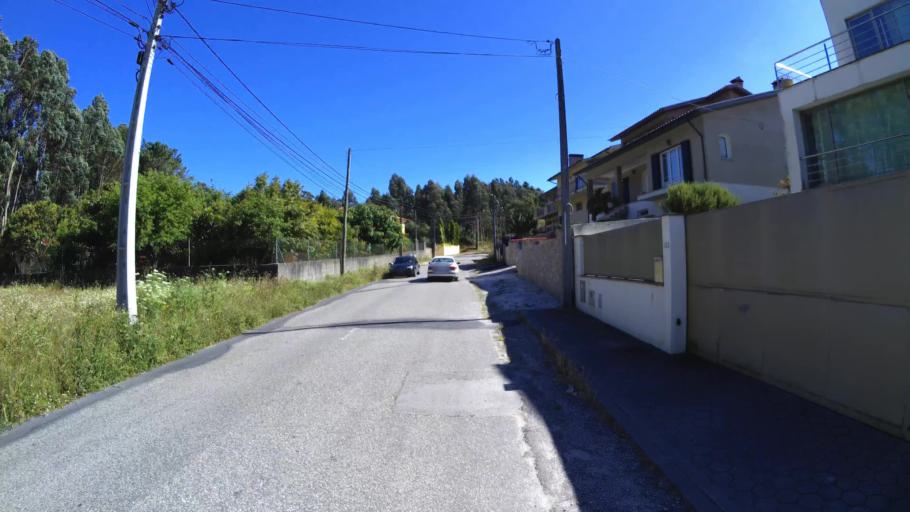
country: PT
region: Aveiro
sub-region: Aveiro
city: Aveiro
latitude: 40.6630
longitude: -8.6205
